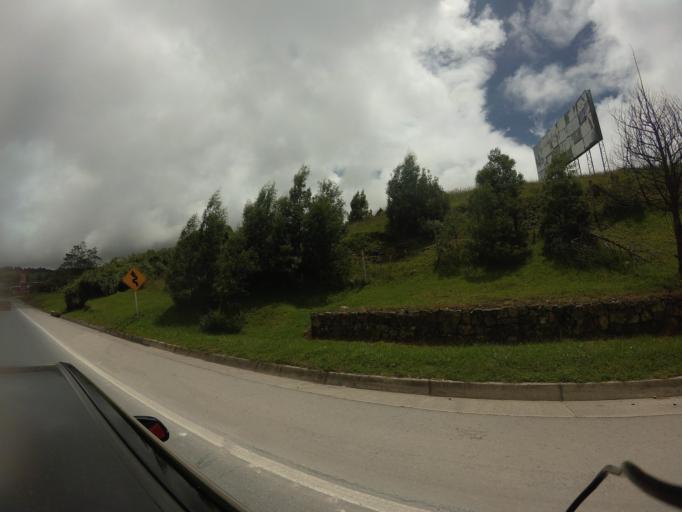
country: CO
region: Boyaca
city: Tunja
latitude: 5.4931
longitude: -73.4023
